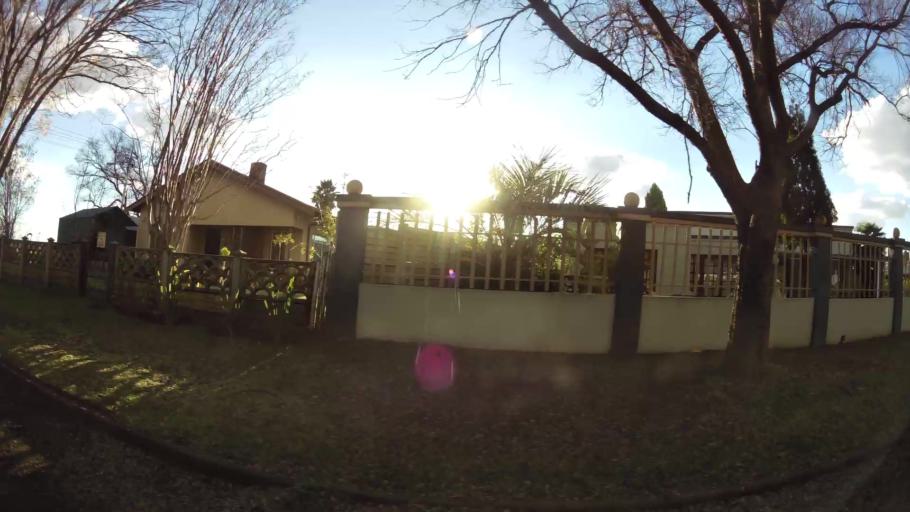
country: ZA
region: North-West
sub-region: Dr Kenneth Kaunda District Municipality
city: Potchefstroom
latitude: -26.7425
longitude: 27.0887
